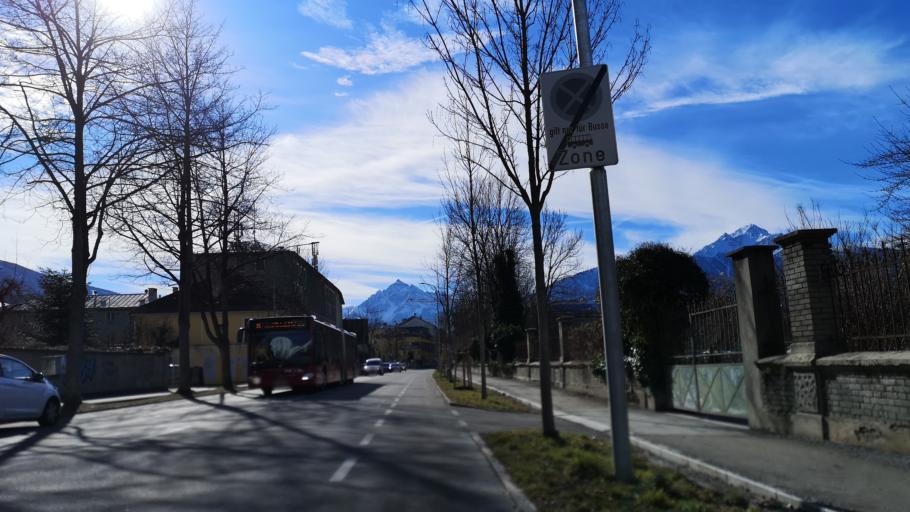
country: AT
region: Tyrol
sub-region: Innsbruck Stadt
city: Innsbruck
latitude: 47.2720
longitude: 11.4002
